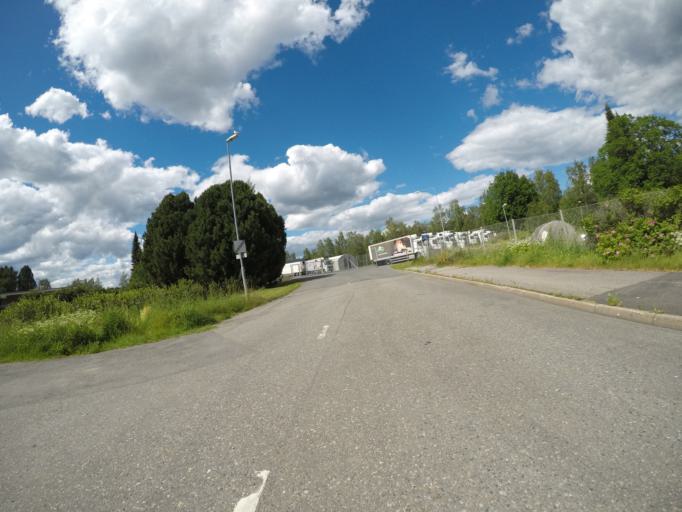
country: FI
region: Haeme
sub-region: Haemeenlinna
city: Haemeenlinna
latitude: 61.0028
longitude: 24.4411
